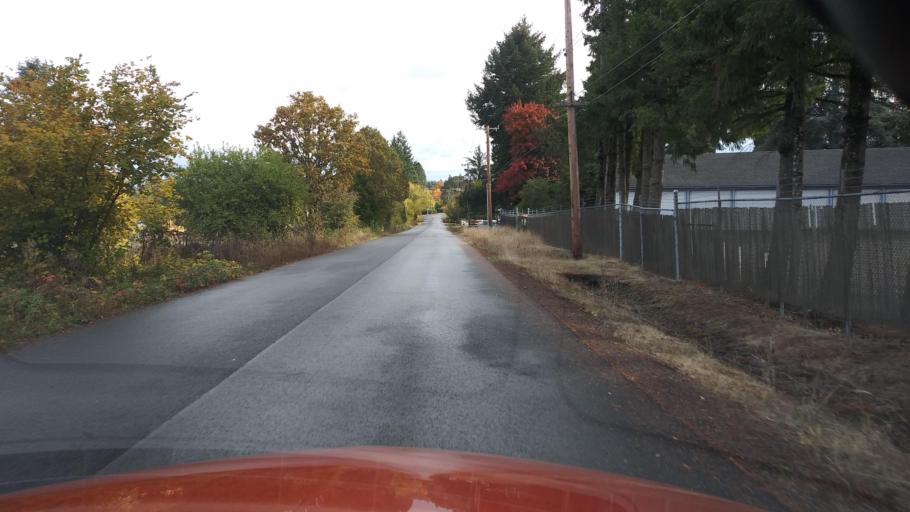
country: US
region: Oregon
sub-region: Washington County
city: Forest Grove
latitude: 45.5327
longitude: -123.1322
